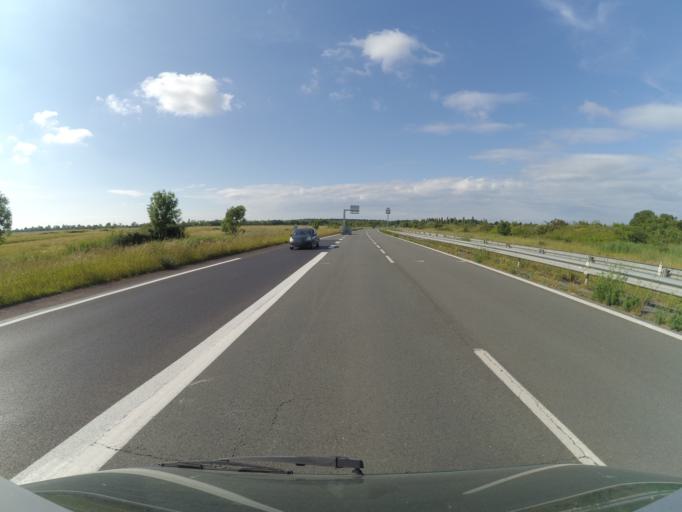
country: FR
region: Poitou-Charentes
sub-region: Departement de la Charente-Maritime
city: Saint-Agnant
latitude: 45.8655
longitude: -0.9693
